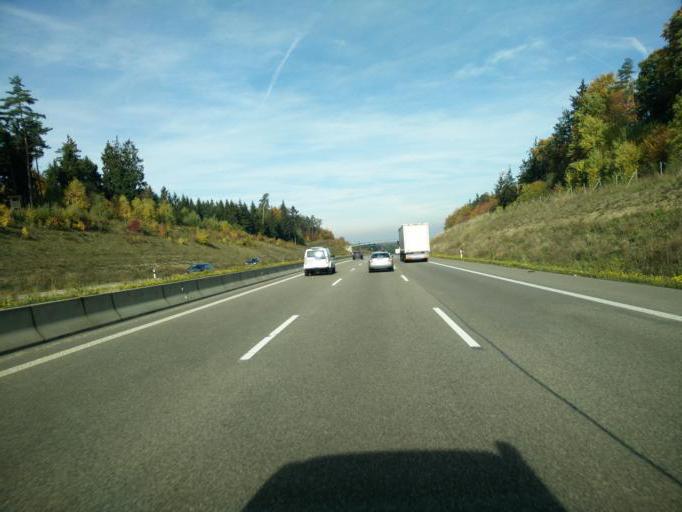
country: DE
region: Baden-Wuerttemberg
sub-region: Karlsruhe Region
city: Tiefenbronn
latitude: 48.8535
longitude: 8.7995
